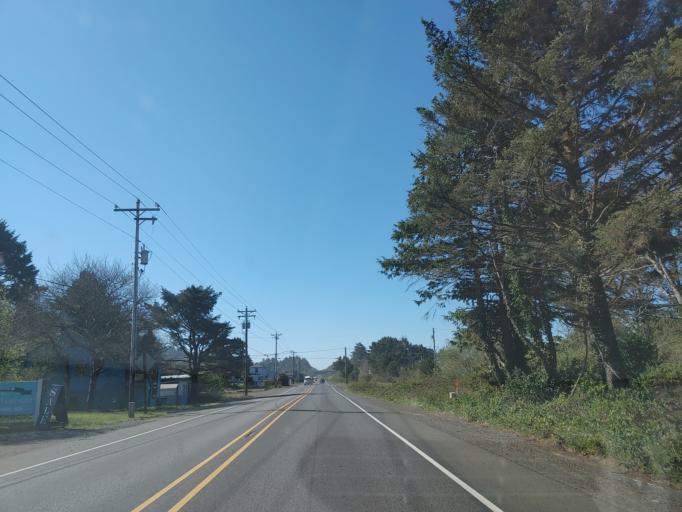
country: US
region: Oregon
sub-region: Tillamook County
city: Rockaway Beach
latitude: 45.5985
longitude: -123.9464
